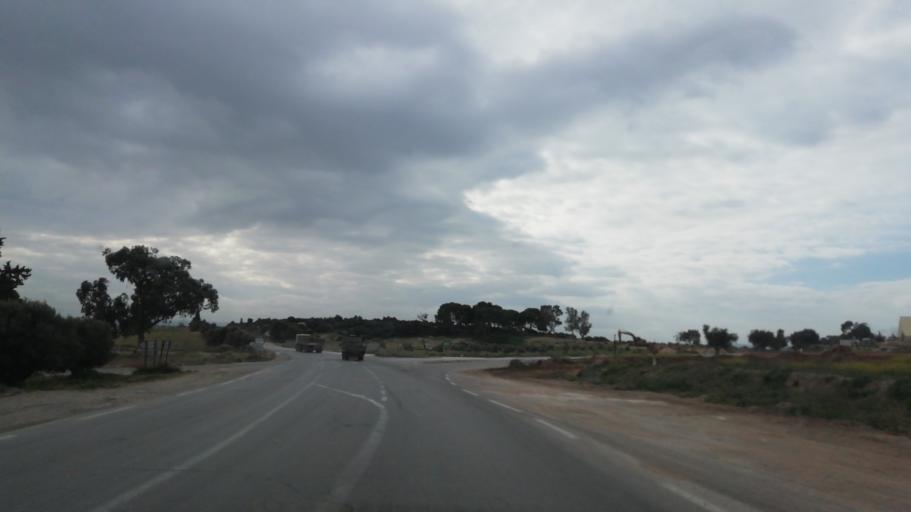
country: DZ
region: Oran
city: Ain el Bya
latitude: 35.7134
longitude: -0.3604
